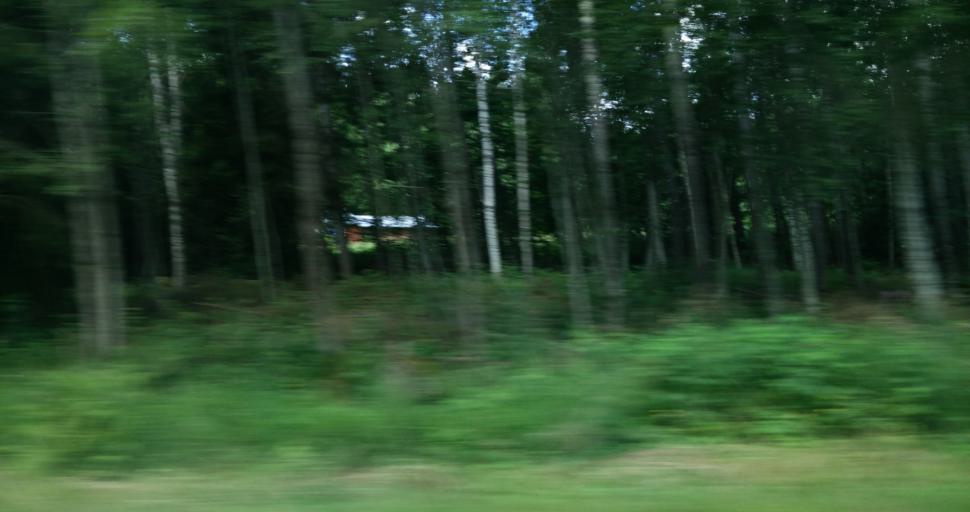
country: SE
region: Vaermland
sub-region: Hagfors Kommun
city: Ekshaerad
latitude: 60.1183
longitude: 13.4508
